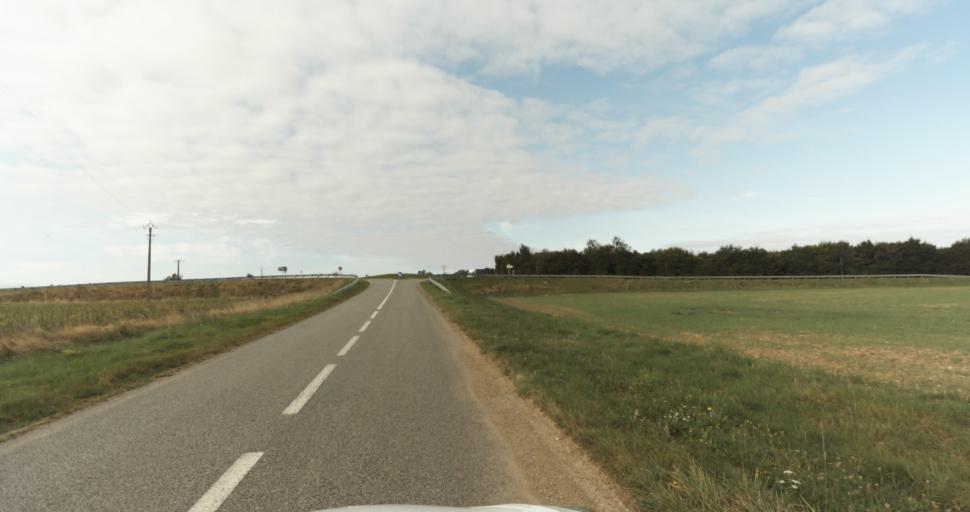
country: FR
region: Haute-Normandie
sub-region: Departement de l'Eure
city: La Madeleine-de-Nonancourt
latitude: 48.8359
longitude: 1.1855
